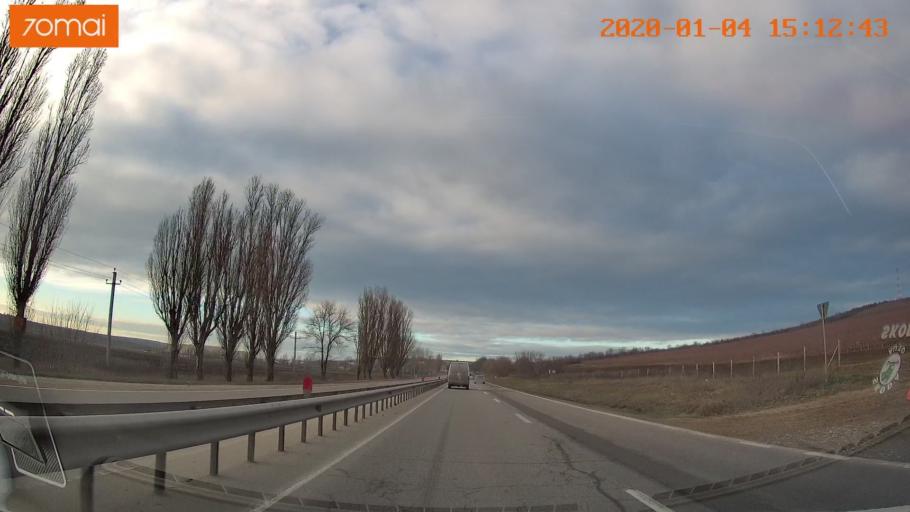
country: MD
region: Chisinau
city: Cricova
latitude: 47.1817
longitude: 28.7924
